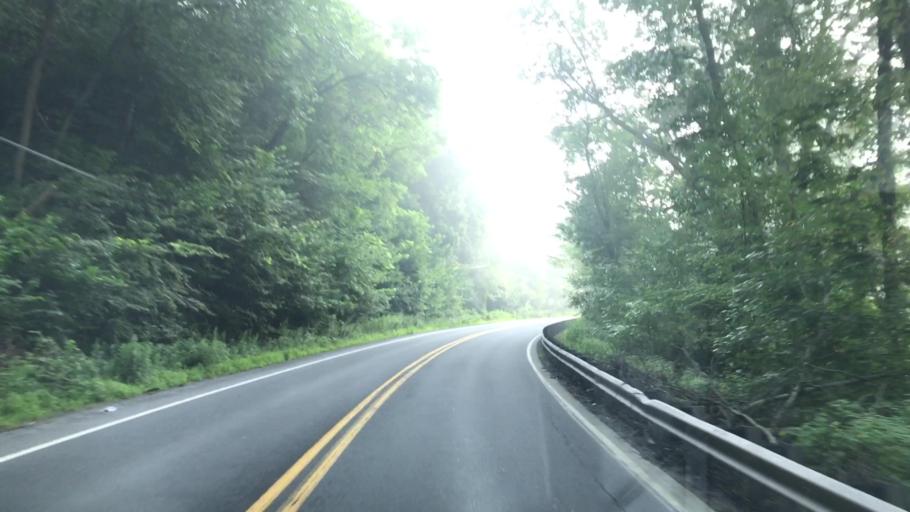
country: US
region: Pennsylvania
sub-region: Wyoming County
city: Factoryville
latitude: 41.6283
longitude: -75.7733
